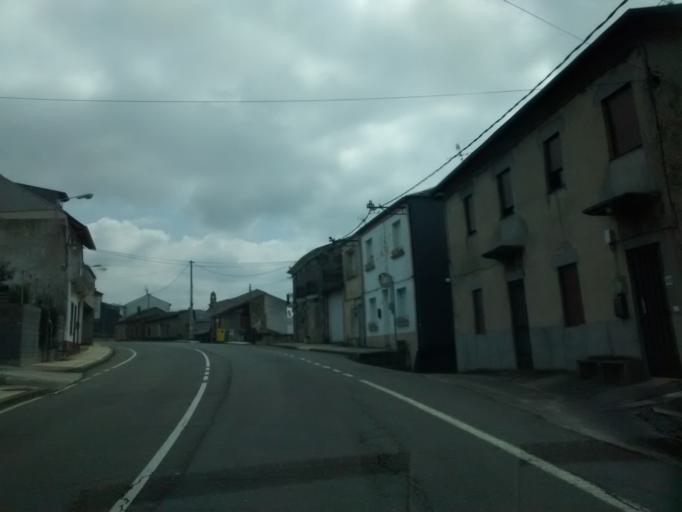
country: ES
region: Galicia
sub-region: Provincia de Ourense
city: Petin
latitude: 42.3463
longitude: -7.1668
